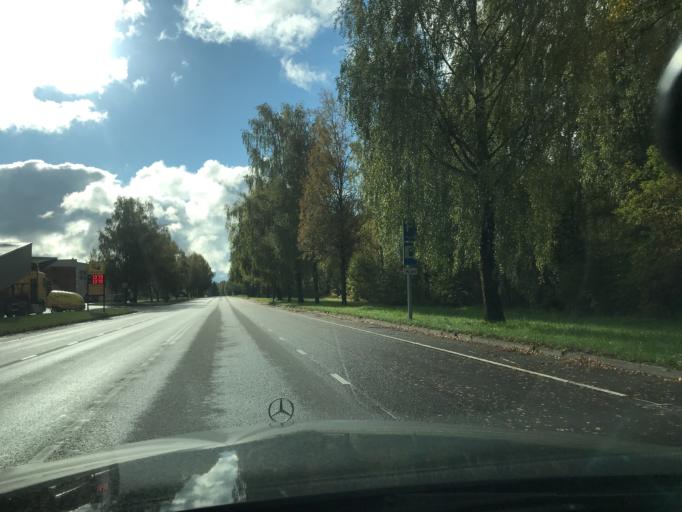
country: EE
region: Valgamaa
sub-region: Torva linn
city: Torva
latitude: 57.9913
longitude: 25.9391
